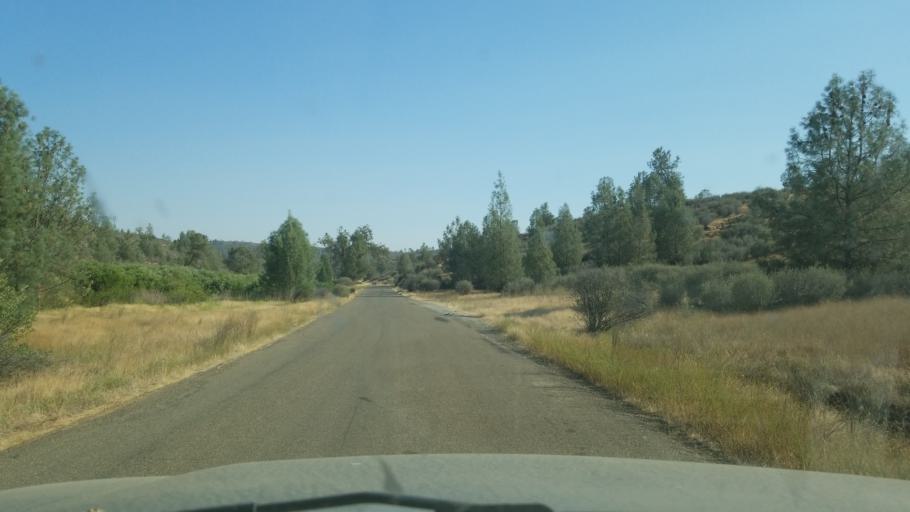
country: US
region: California
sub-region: Tuolumne County
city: Jamestown
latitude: 37.8560
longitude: -120.4535
